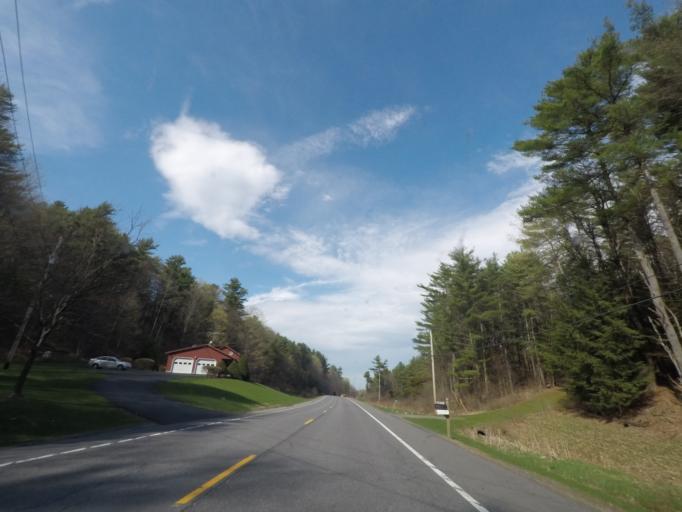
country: US
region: New York
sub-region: Albany County
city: Voorheesville
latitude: 42.5329
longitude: -73.9461
